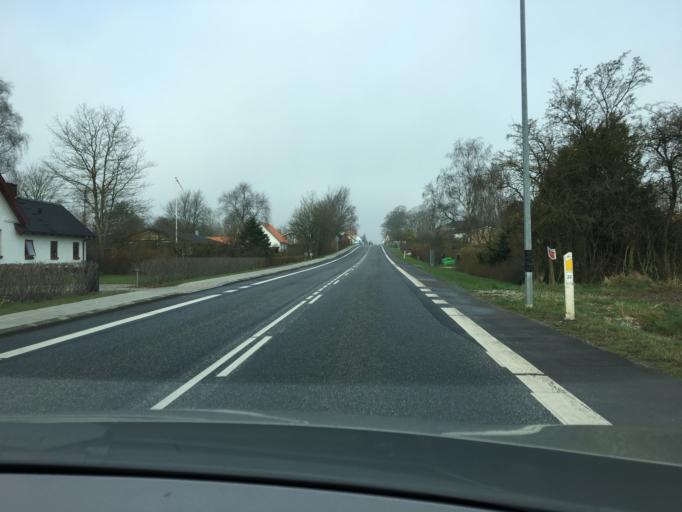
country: DK
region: South Denmark
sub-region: Vejle Kommune
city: Give
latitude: 55.8274
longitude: 9.3236
